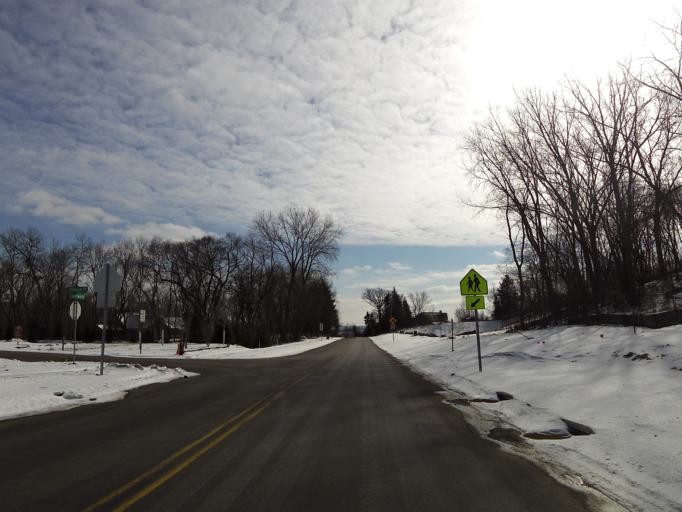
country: US
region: Minnesota
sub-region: Hennepin County
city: Eden Prairie
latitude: 44.8221
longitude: -93.4853
